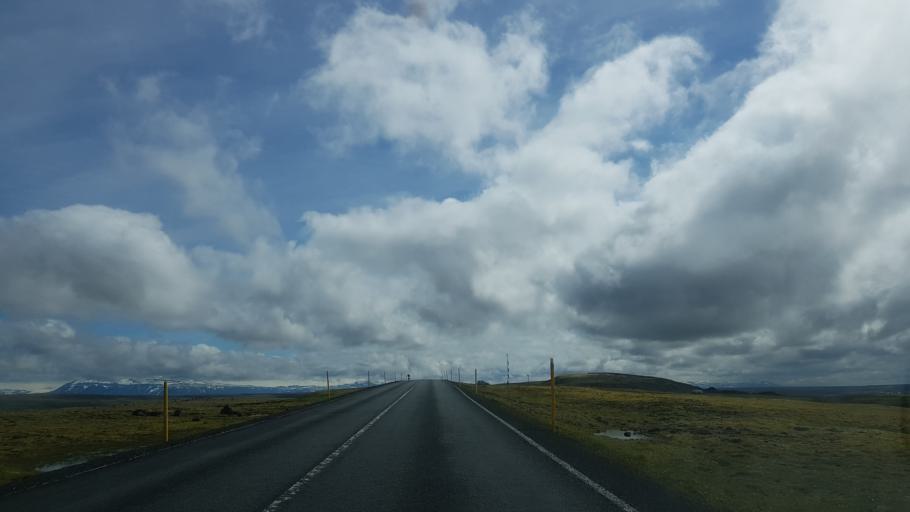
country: IS
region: West
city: Borgarnes
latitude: 64.9923
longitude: -21.0606
